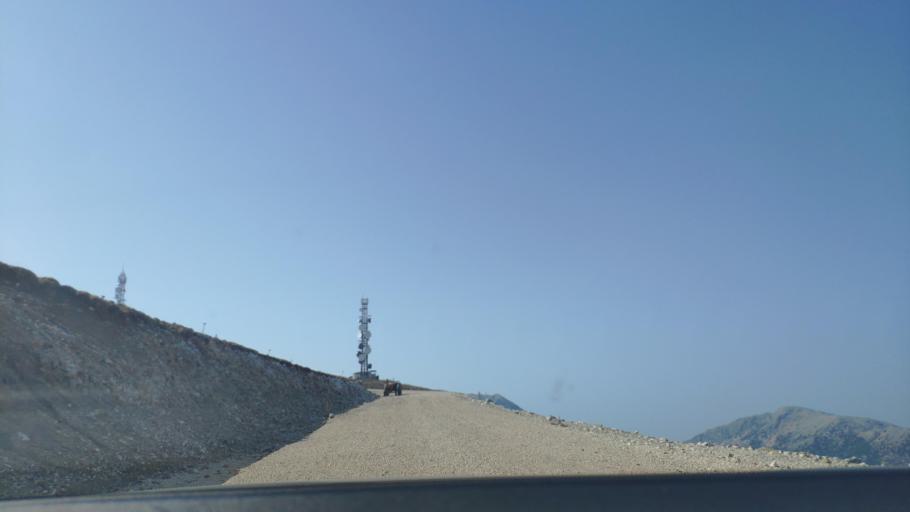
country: GR
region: West Greece
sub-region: Nomos Aitolias kai Akarnanias
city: Monastirakion
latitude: 38.8095
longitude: 20.9798
